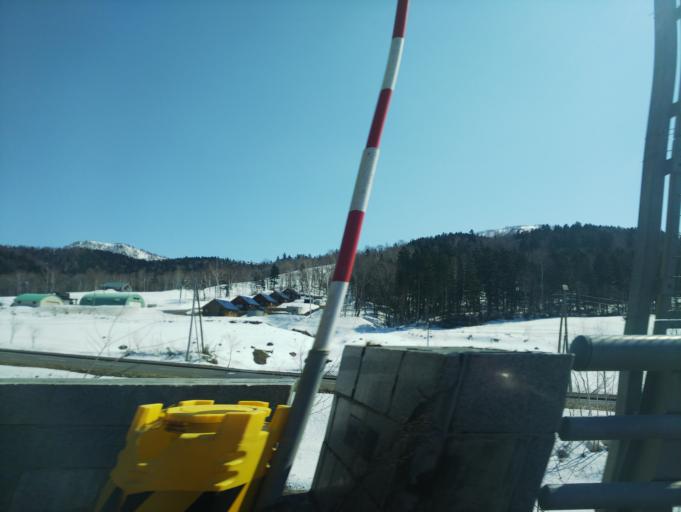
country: JP
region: Hokkaido
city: Nayoro
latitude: 44.7207
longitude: 142.2703
